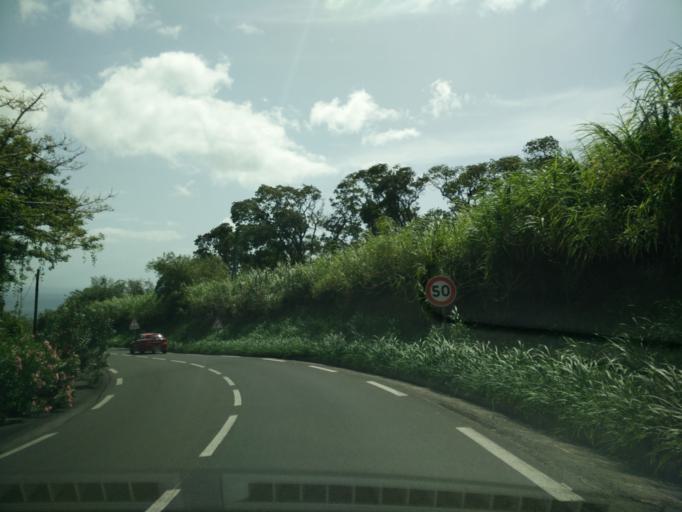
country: MQ
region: Martinique
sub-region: Martinique
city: Le Morne-Rouge
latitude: 14.7610
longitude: -61.1572
